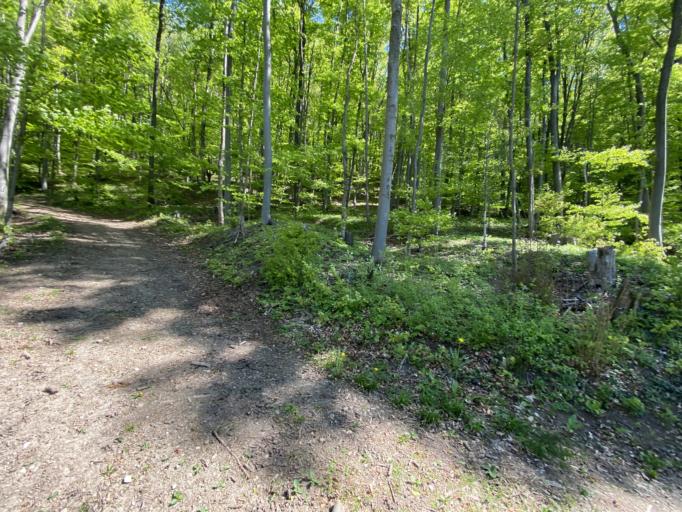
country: AT
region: Lower Austria
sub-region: Politischer Bezirk Modling
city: Breitenfurt bei Wien
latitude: 48.1074
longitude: 16.1608
